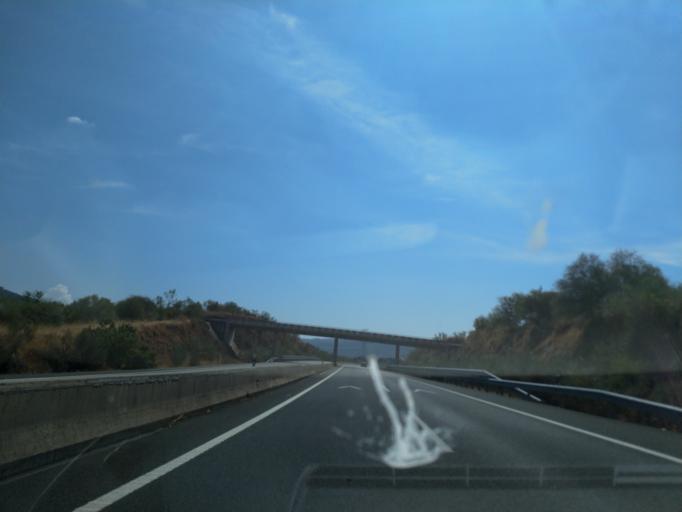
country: ES
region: Extremadura
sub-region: Provincia de Caceres
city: Casas de Miravete
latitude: 39.7448
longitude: -5.7261
